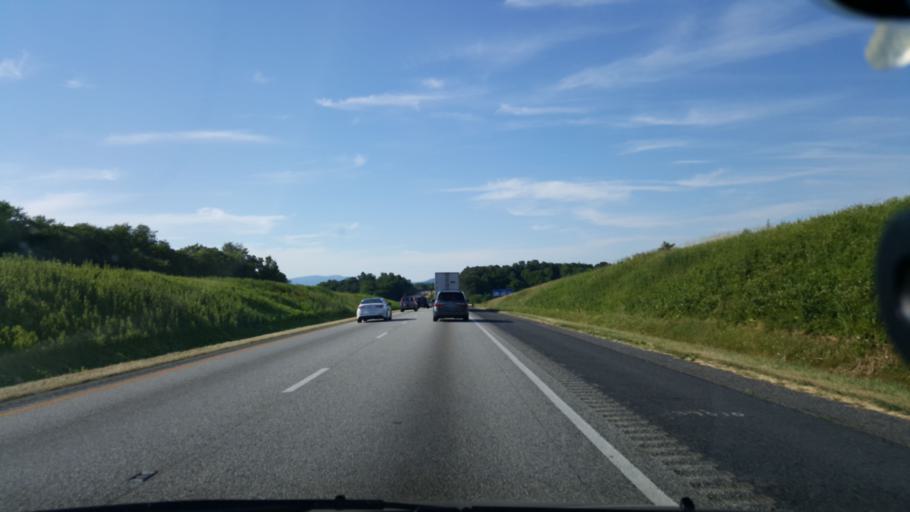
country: US
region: Virginia
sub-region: Augusta County
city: Weyers Cave
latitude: 38.3276
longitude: -78.9318
